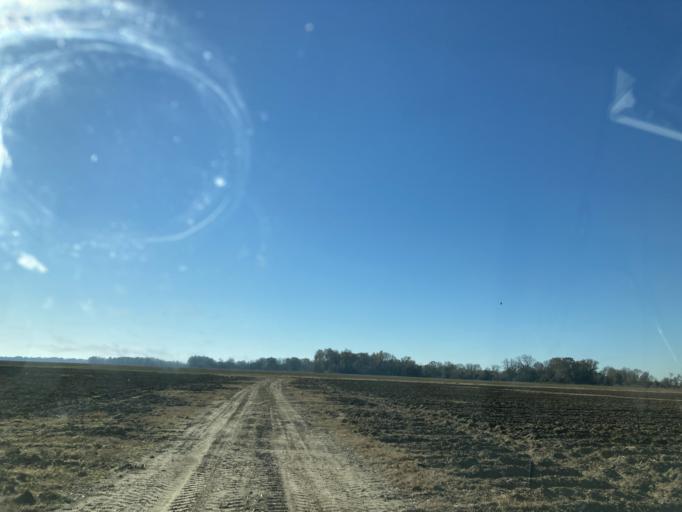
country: US
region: Mississippi
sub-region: Sharkey County
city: Rolling Fork
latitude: 32.8587
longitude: -90.6938
